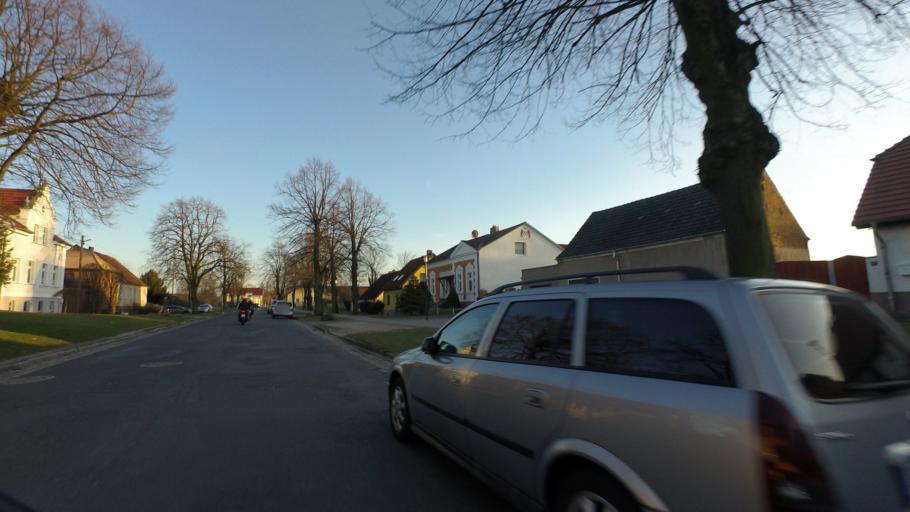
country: DE
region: Berlin
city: Hellersdorf
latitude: 52.5448
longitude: 13.6388
